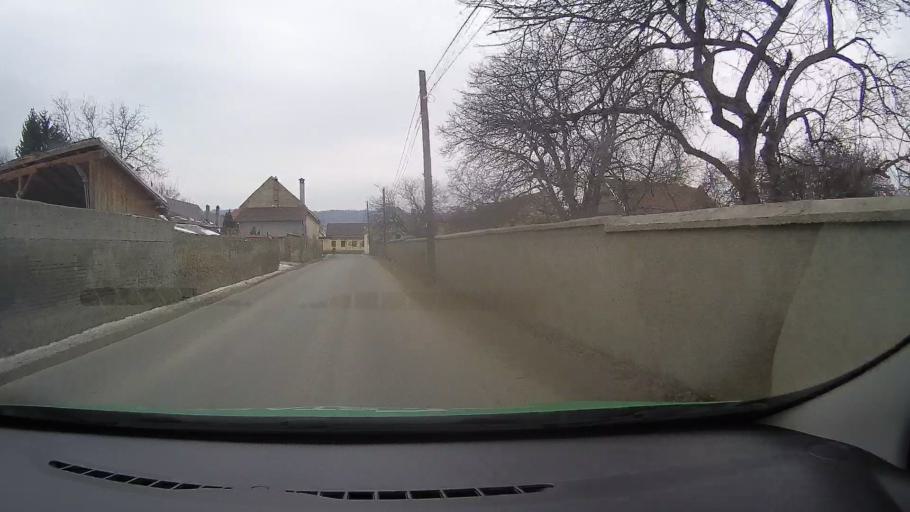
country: RO
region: Brasov
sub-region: Comuna Vulcan
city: Vulcan
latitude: 45.6349
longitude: 25.4247
